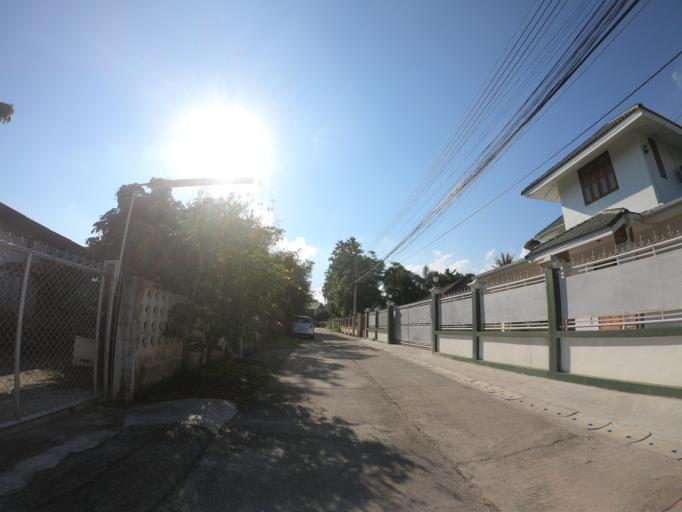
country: TH
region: Chiang Mai
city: Chiang Mai
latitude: 18.7532
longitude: 98.9686
